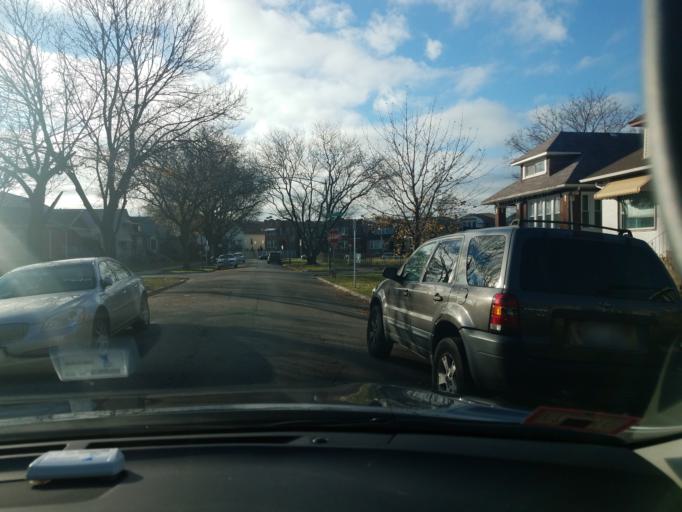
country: US
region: Illinois
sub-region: Cook County
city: Lincolnwood
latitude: 41.9644
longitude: -87.7316
